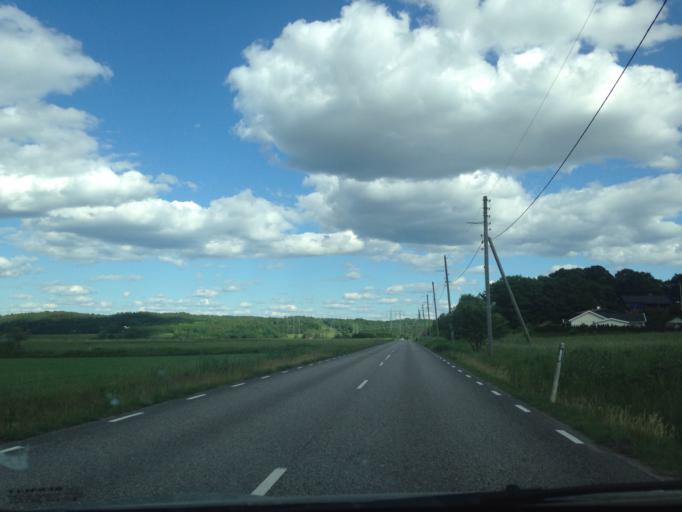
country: SE
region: Vaestra Goetaland
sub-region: Goteborg
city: Goeteborg
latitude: 57.7719
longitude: 11.9222
